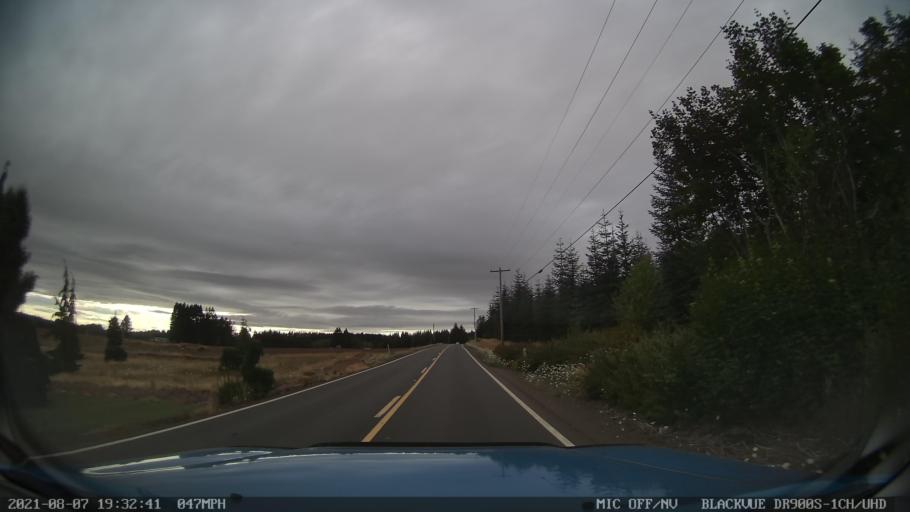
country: US
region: Oregon
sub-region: Linn County
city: Lyons
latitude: 44.9019
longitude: -122.6467
